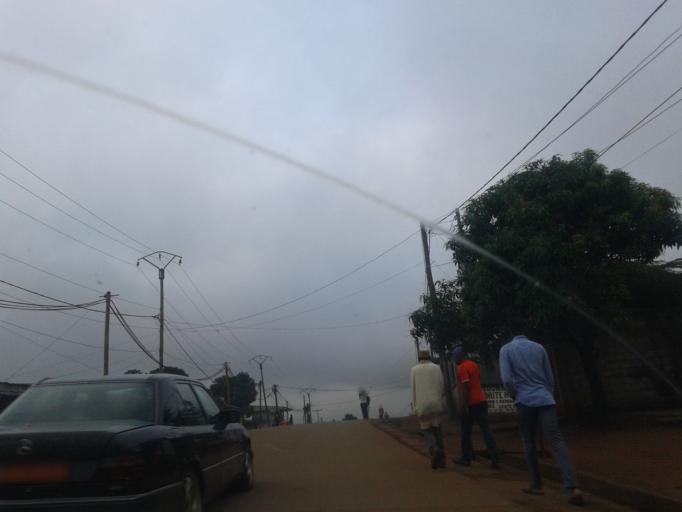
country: CM
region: Centre
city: Yaounde
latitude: 3.8948
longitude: 11.5300
